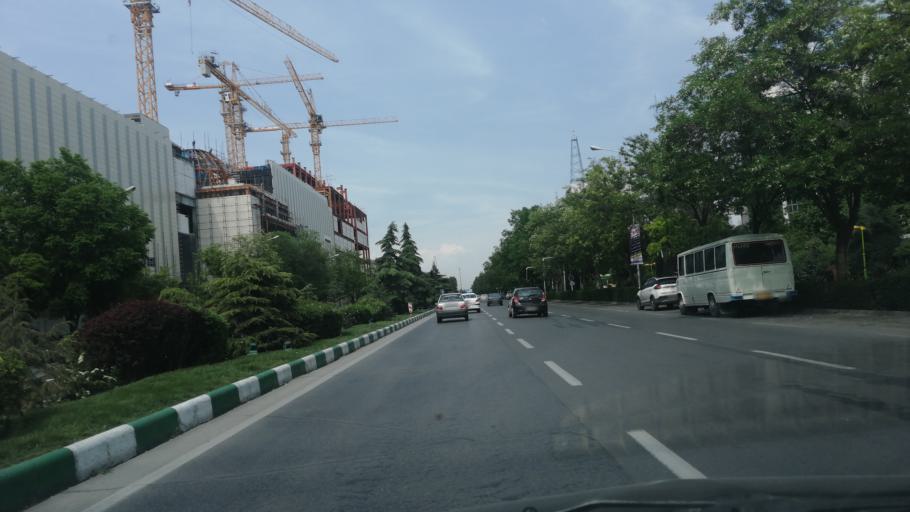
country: IR
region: Razavi Khorasan
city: Mashhad
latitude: 36.3156
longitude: 59.5612
